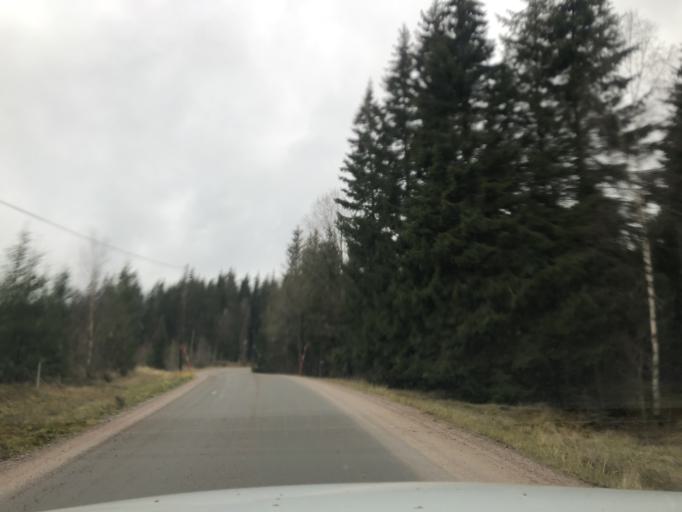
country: SE
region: Vaestra Goetaland
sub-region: Ulricehamns Kommun
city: Ulricehamn
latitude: 57.8635
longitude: 13.5643
